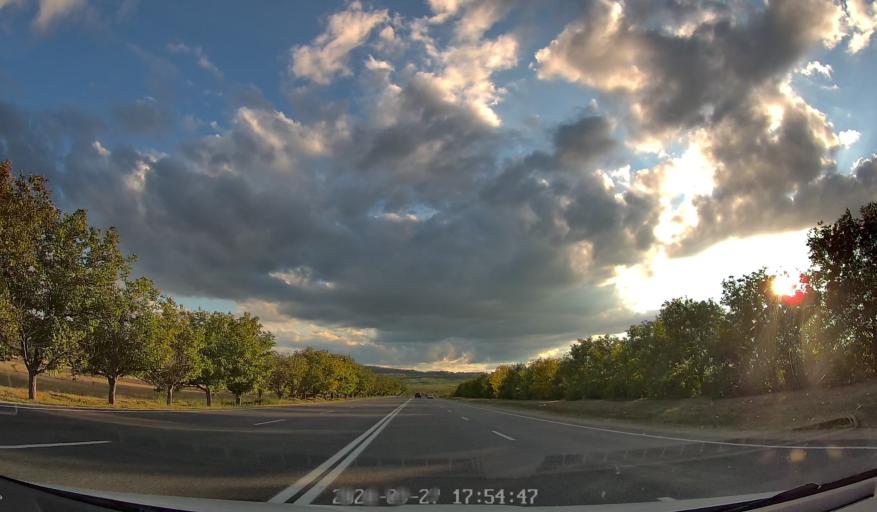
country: MD
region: Orhei
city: Orhei
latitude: 47.2853
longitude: 28.8043
